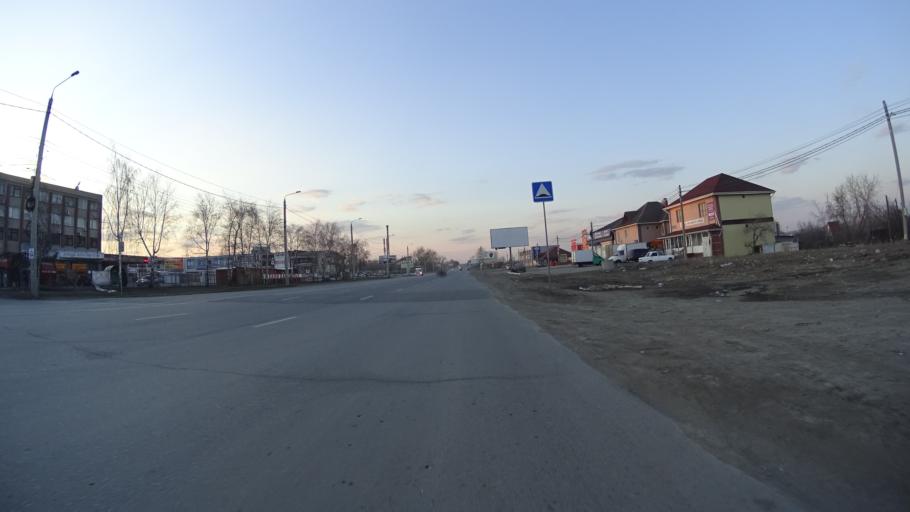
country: RU
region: Chelyabinsk
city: Novosineglazovskiy
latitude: 55.0931
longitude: 61.3882
